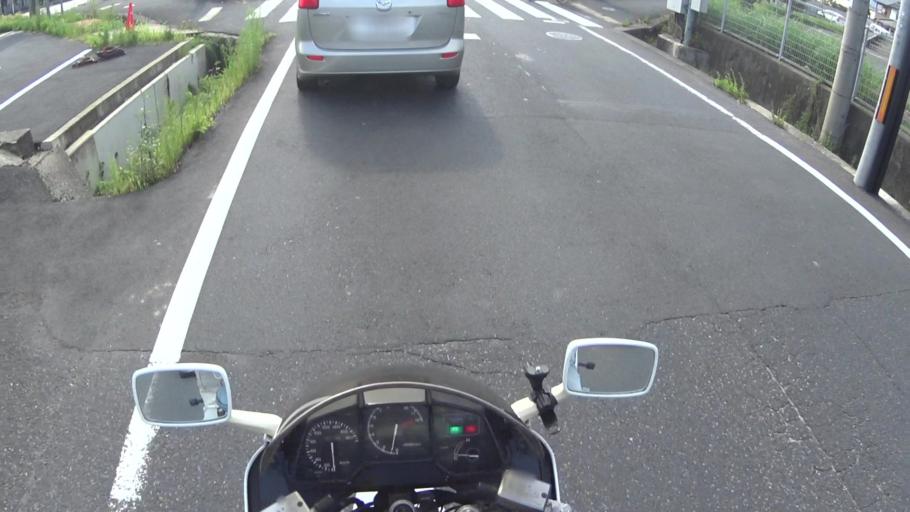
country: JP
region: Kyoto
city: Miyazu
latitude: 35.5989
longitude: 135.0883
